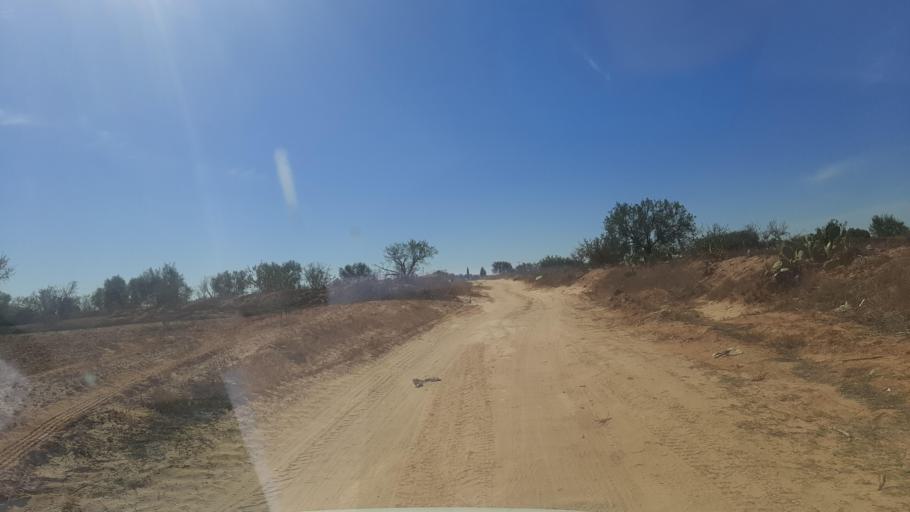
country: TN
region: Safaqis
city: Sfax
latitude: 34.8328
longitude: 10.5570
